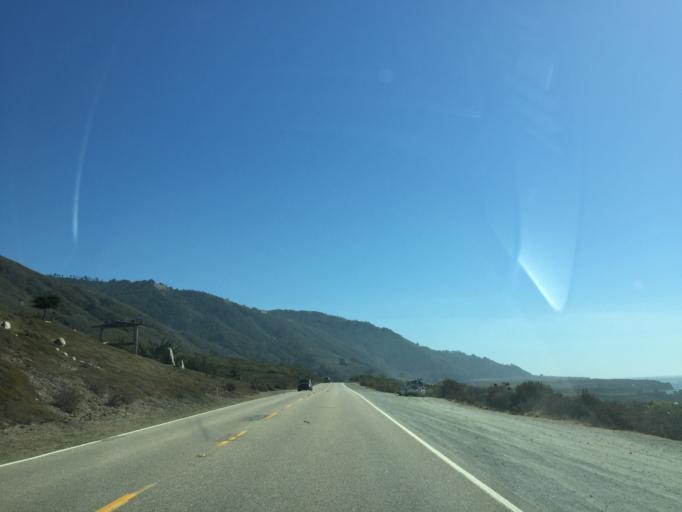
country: US
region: California
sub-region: Monterey County
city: King City
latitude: 35.9464
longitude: -121.4769
